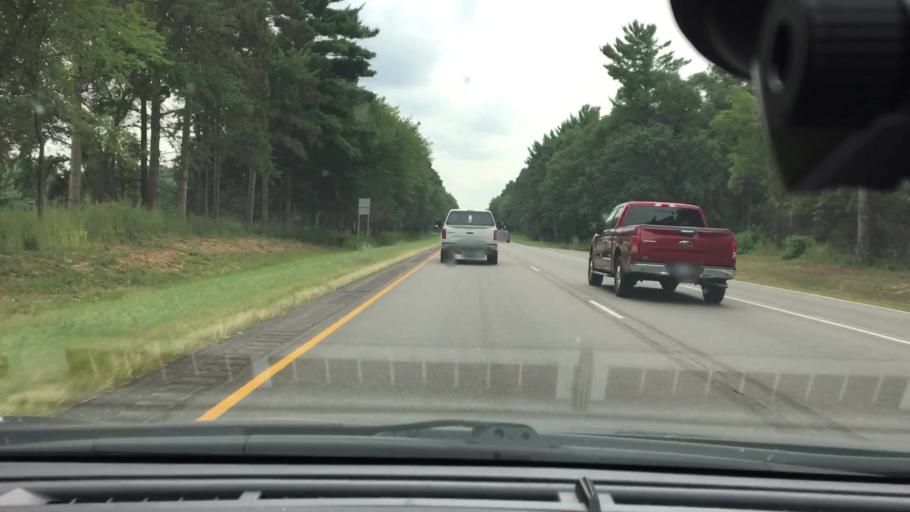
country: US
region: Minnesota
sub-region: Sherburne County
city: Zimmerman
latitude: 45.4761
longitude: -93.5828
